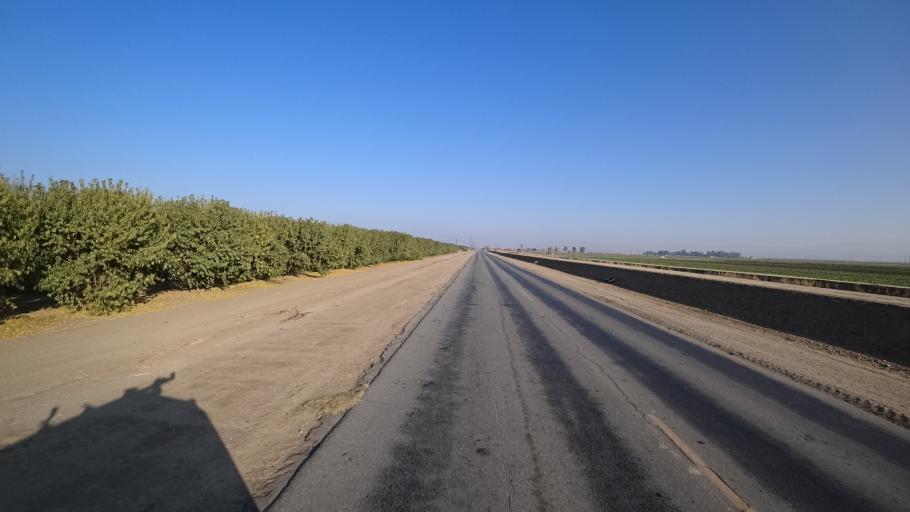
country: US
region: California
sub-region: Kern County
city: Greenfield
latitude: 35.2553
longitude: -118.9854
